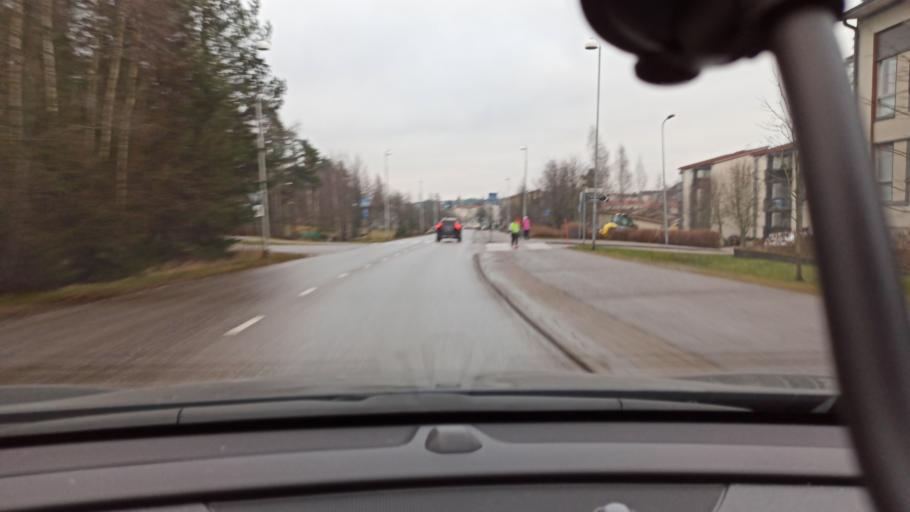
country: FI
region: Uusimaa
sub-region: Helsinki
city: Kirkkonummi
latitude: 60.1300
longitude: 24.4335
